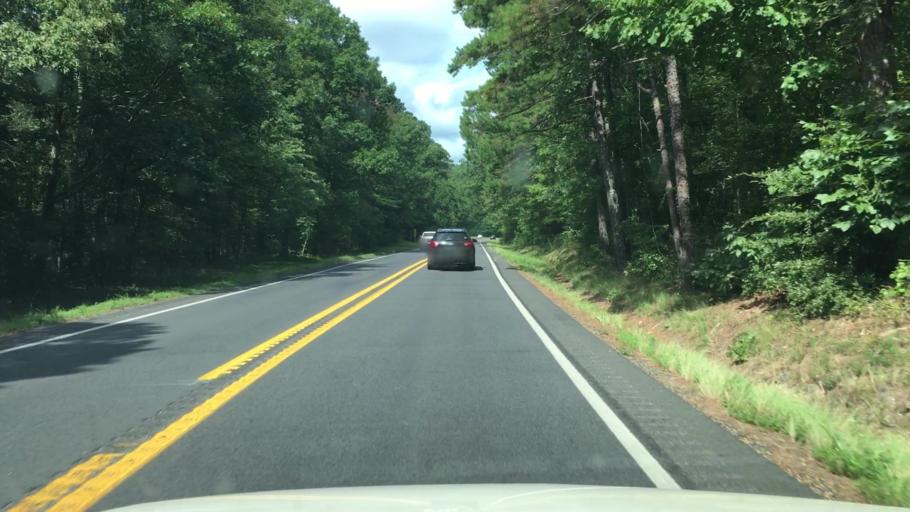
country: US
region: Arkansas
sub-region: Garland County
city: Lake Hamilton
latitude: 34.3605
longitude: -93.1715
